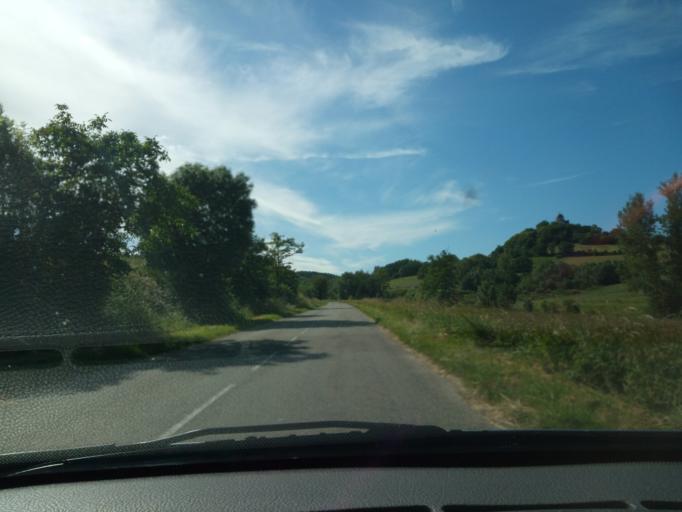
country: FR
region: Midi-Pyrenees
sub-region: Departement du Lot
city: Castelnau-Montratier
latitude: 44.2607
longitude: 1.3593
